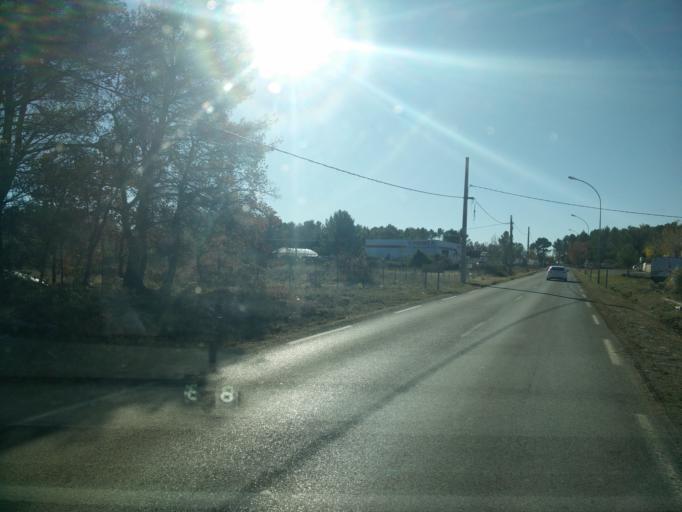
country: FR
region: Provence-Alpes-Cote d'Azur
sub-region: Departement du Var
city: Aups
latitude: 43.6153
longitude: 6.2193
